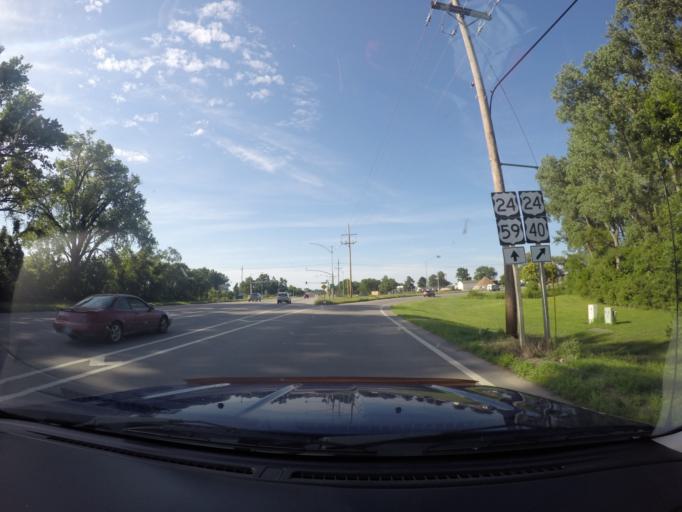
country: US
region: Kansas
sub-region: Douglas County
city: Lawrence
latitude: 38.9996
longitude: -95.2333
